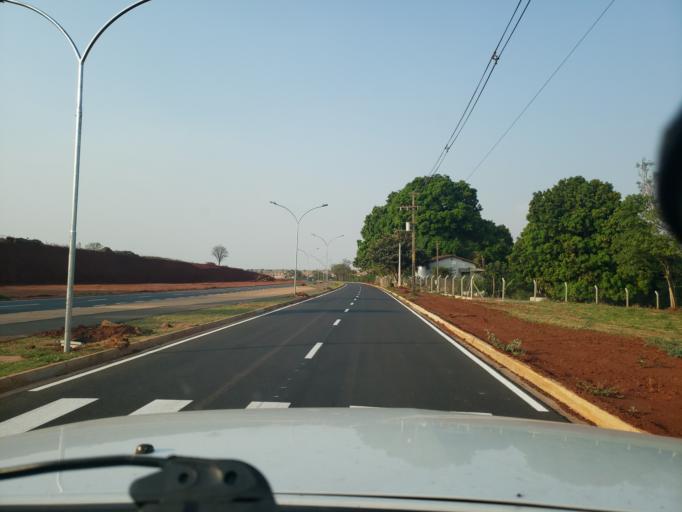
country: BR
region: Sao Paulo
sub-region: Moji-Guacu
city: Mogi-Gaucu
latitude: -22.3237
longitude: -46.9486
